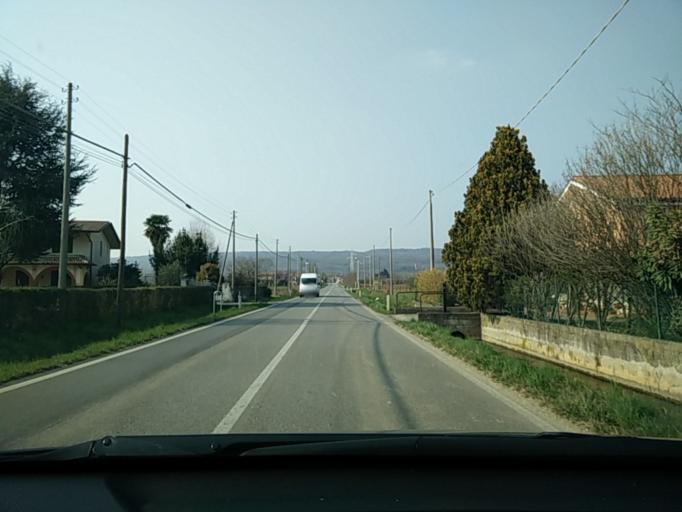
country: IT
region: Veneto
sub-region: Provincia di Treviso
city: Selva del Montello
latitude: 45.7735
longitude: 12.1421
